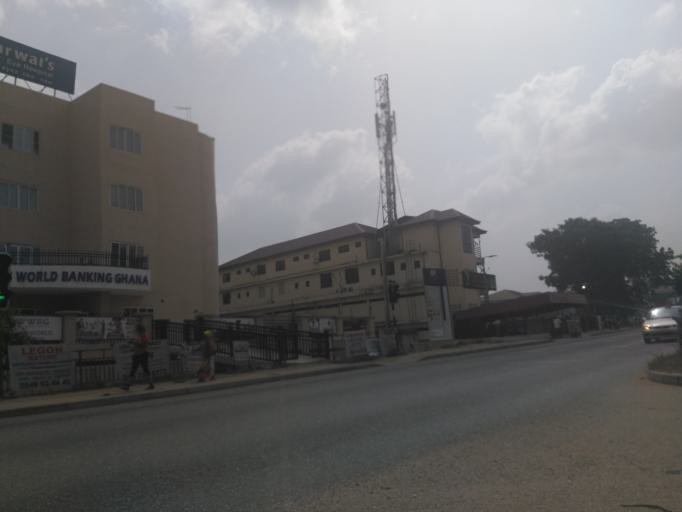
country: GH
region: Greater Accra
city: Dome
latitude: 5.6061
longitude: -0.2260
